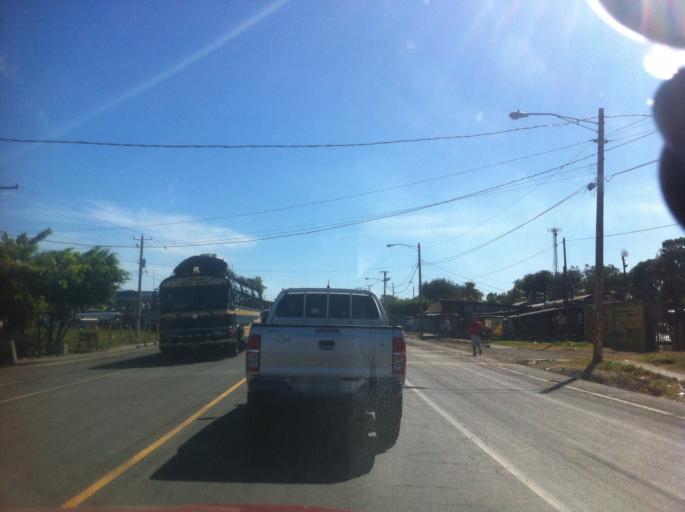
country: NI
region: Managua
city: Tipitapa
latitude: 12.3096
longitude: -86.0547
